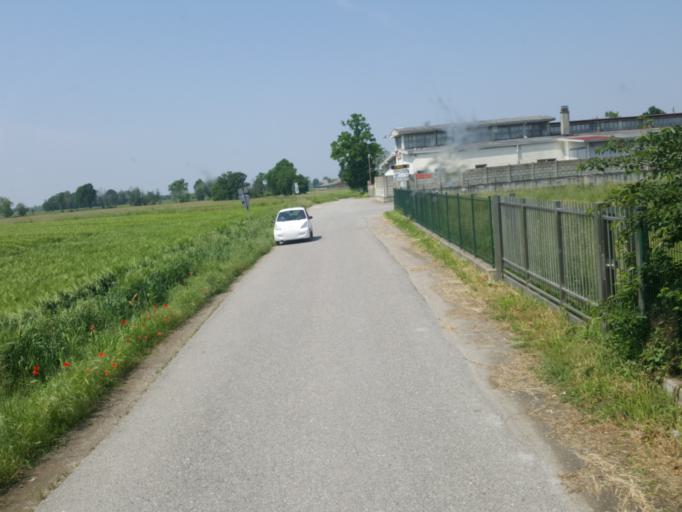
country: IT
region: Lombardy
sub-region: Provincia di Cremona
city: Dovera
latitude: 45.3766
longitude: 9.5419
